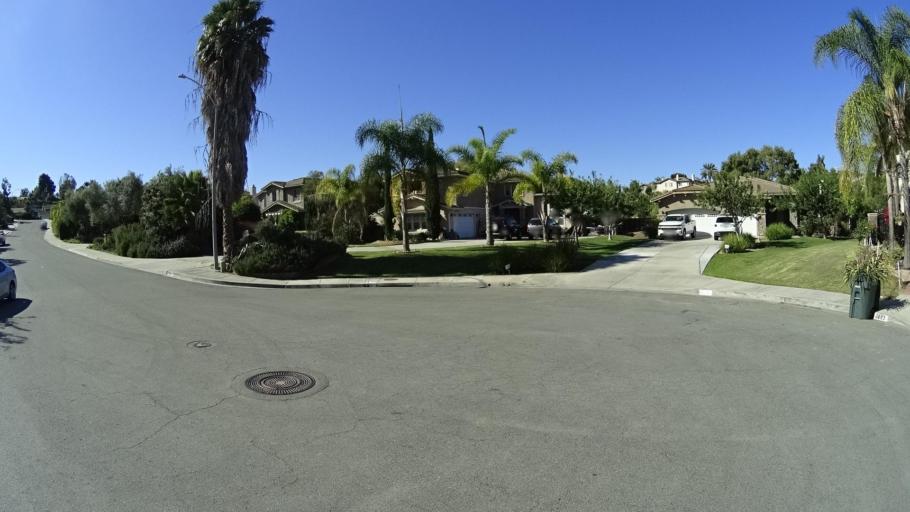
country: US
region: California
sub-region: San Diego County
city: Bonita
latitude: 32.6736
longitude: -117.0108
